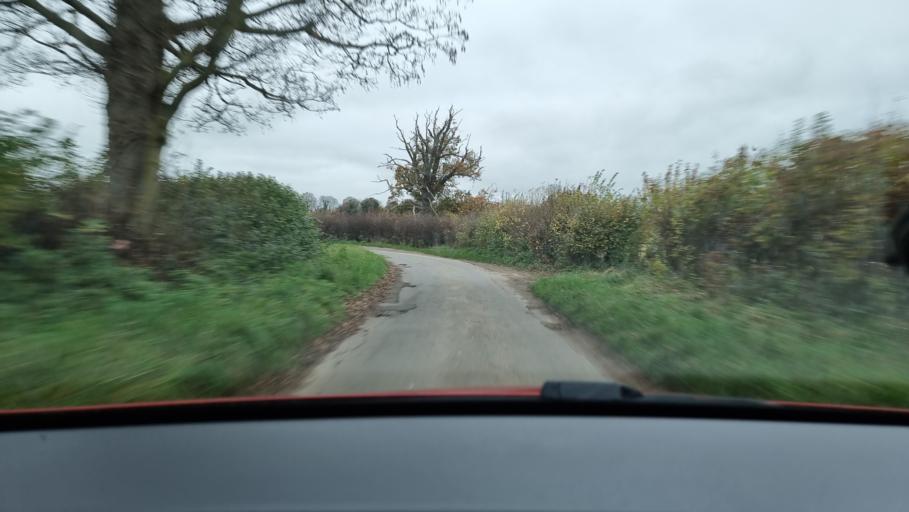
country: GB
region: England
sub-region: Oxfordshire
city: Woodstock
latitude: 51.8712
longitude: -1.3074
